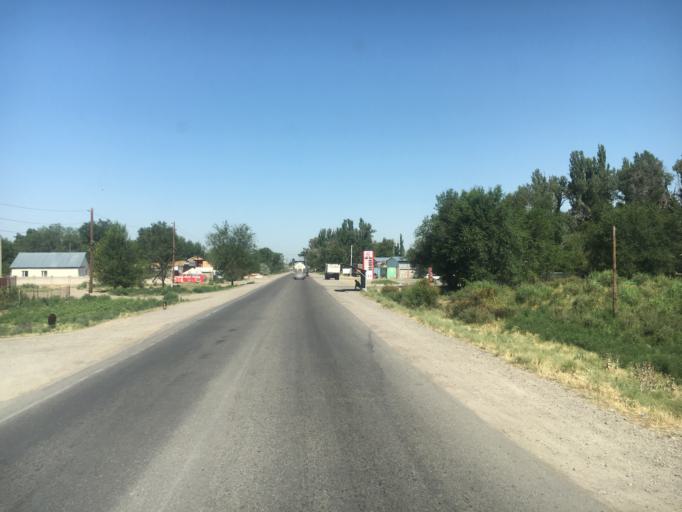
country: KZ
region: Zhambyl
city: Taraz
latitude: 42.9427
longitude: 71.4137
